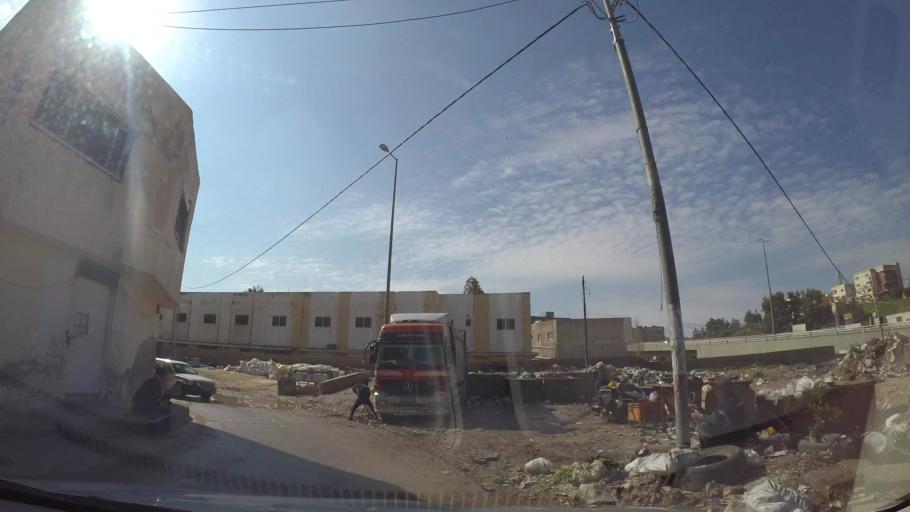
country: JO
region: Amman
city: Al Jubayhah
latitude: 32.0662
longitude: 35.8391
